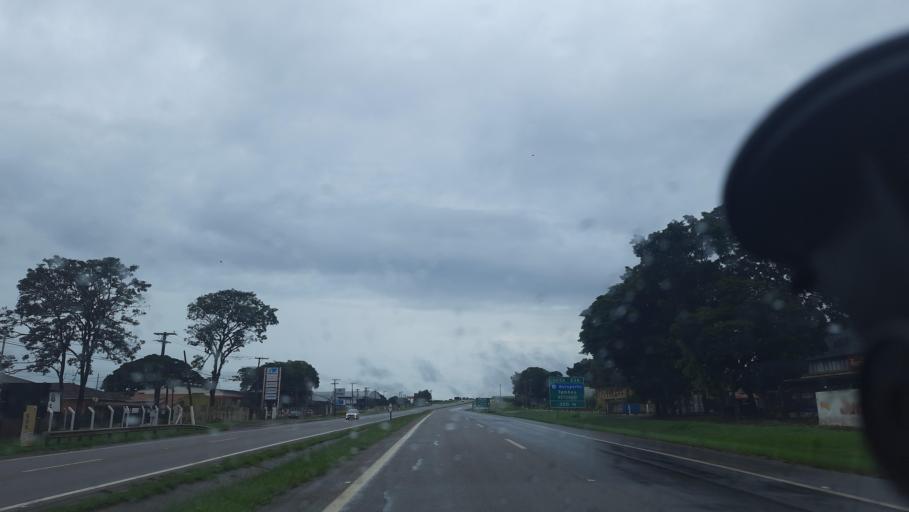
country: BR
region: Sao Paulo
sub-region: Casa Branca
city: Casa Branca
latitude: -21.7810
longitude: -47.0627
